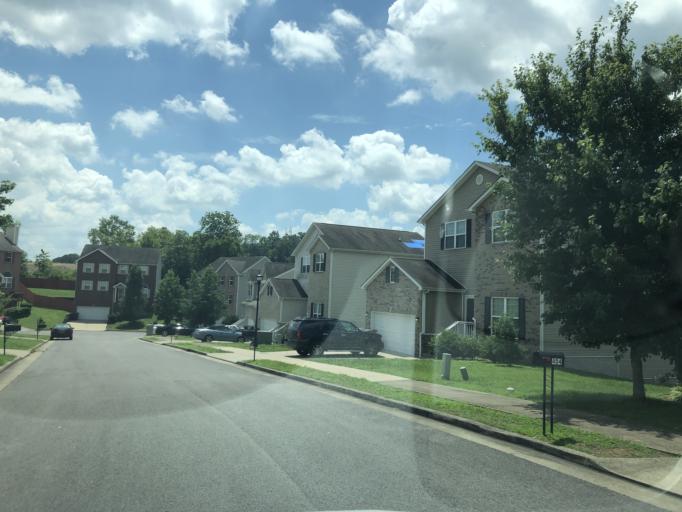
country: US
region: Tennessee
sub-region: Rutherford County
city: La Vergne
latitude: 36.0420
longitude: -86.6197
